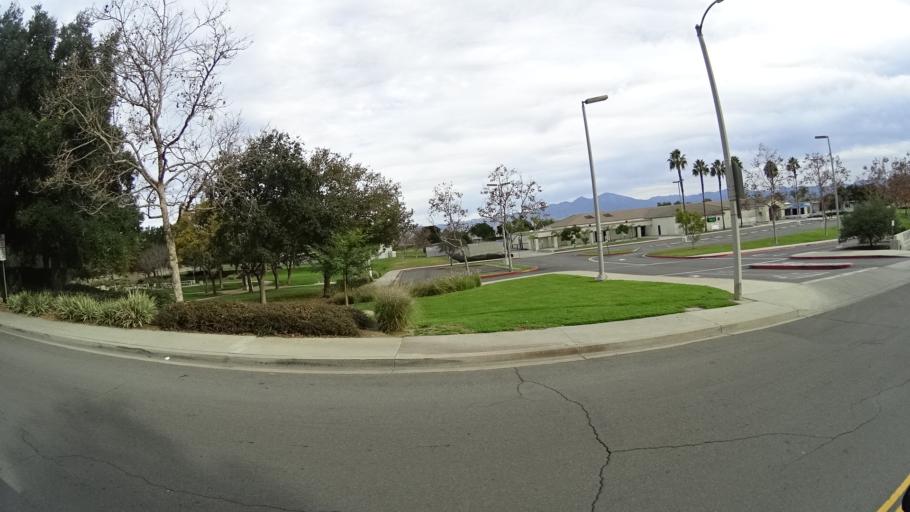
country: US
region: California
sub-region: Orange County
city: Aliso Viejo
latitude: 33.5753
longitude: -117.7359
